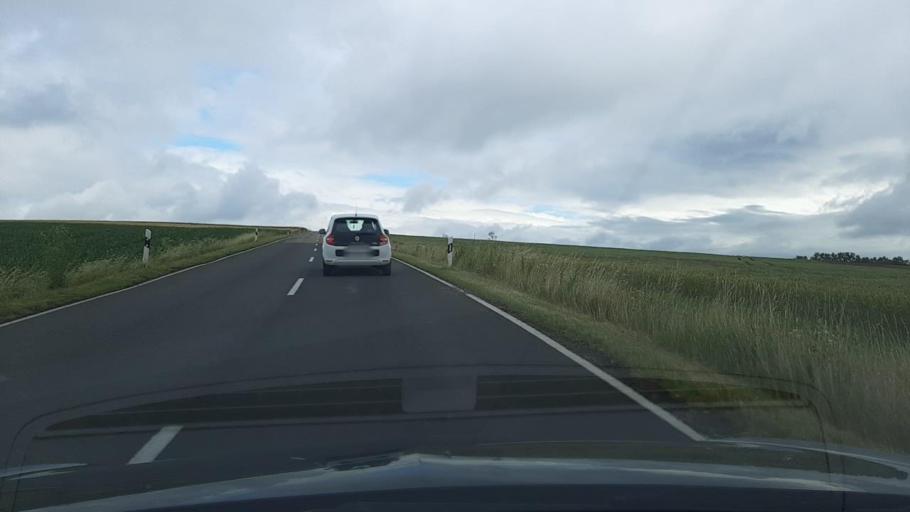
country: DE
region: Rheinland-Pfalz
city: Kerben
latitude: 50.3180
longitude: 7.3864
